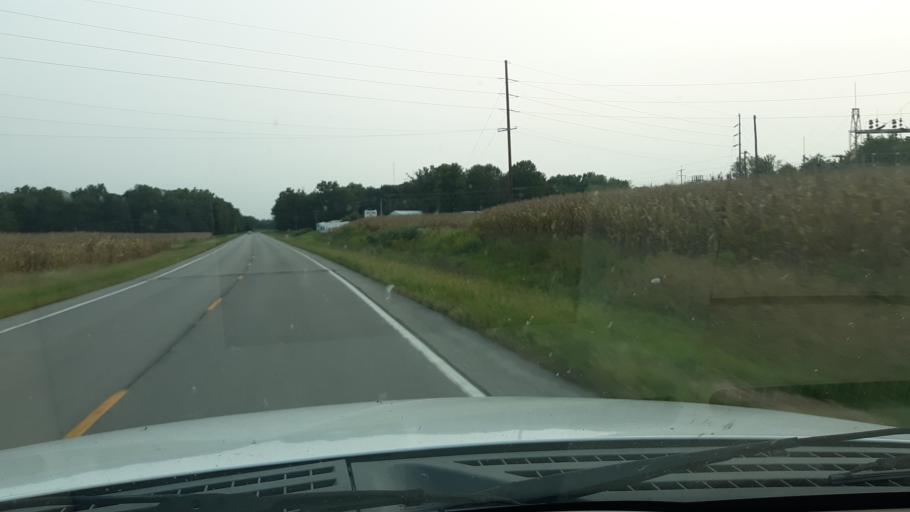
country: US
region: Illinois
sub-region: White County
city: Norris City
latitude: 37.9772
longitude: -88.3182
